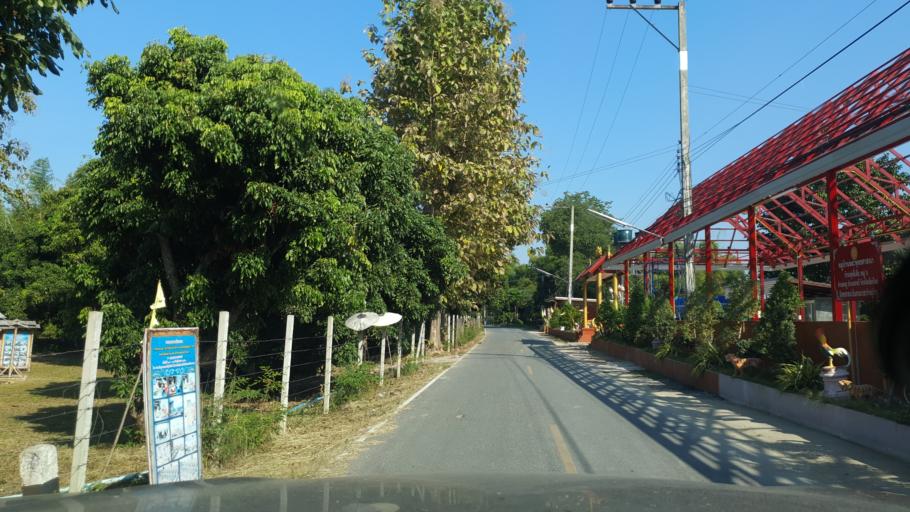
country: TH
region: Chiang Mai
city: Saraphi
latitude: 18.7035
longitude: 99.0762
